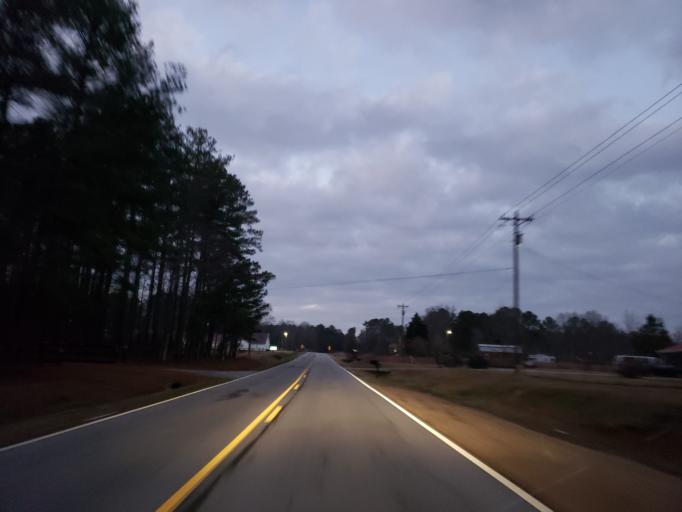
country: US
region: Georgia
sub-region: Carroll County
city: Temple
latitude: 33.7802
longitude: -85.0625
